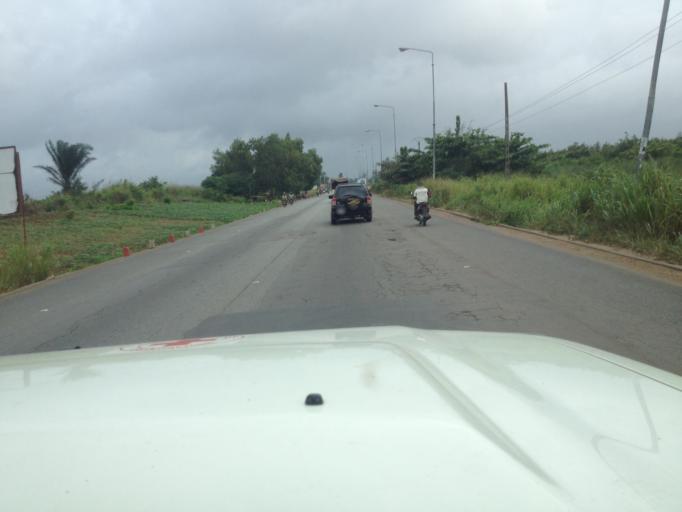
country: BJ
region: Queme
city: Porto-Novo
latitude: 6.4471
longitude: 2.6212
